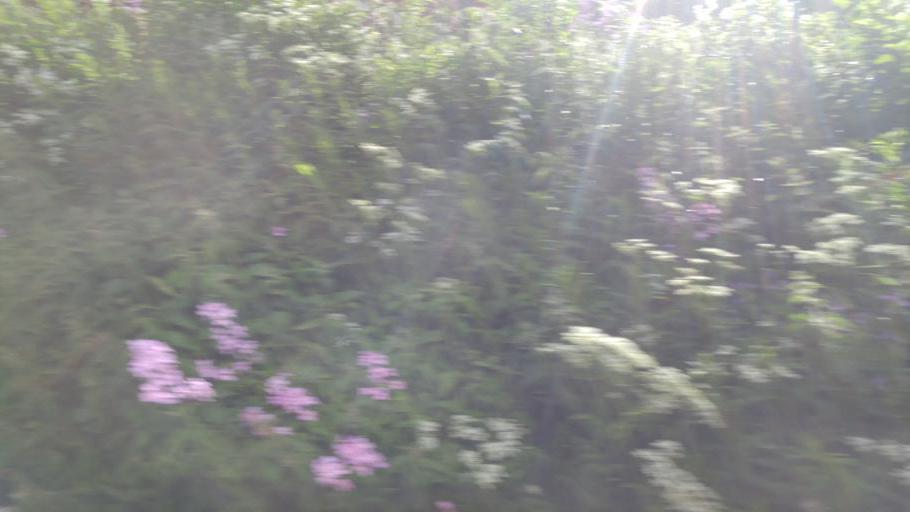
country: NO
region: Nord-Trondelag
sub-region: Meraker
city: Meraker
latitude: 63.4133
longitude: 11.7554
